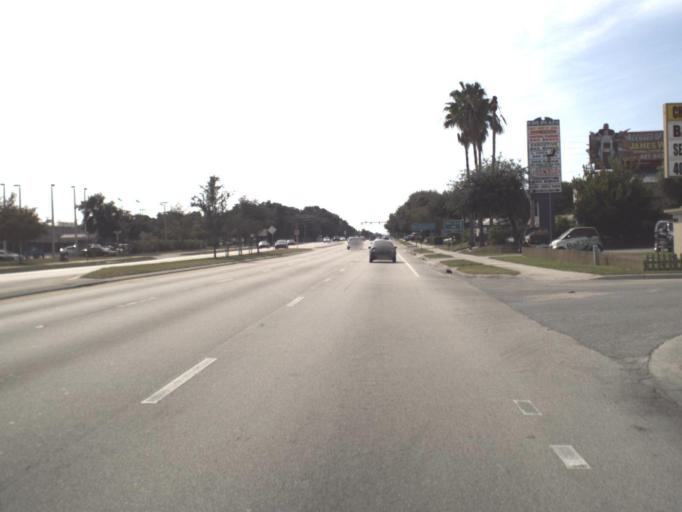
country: US
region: Florida
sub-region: Orange County
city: Holden Heights
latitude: 28.5046
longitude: -81.4176
